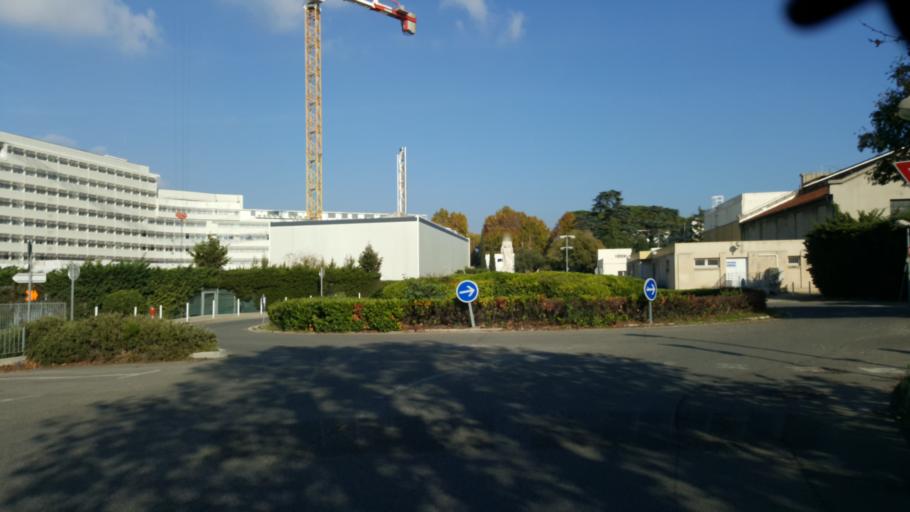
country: FR
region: Provence-Alpes-Cote d'Azur
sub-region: Departement des Bouches-du-Rhone
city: Marseille 09
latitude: 43.2611
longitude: 5.4099
